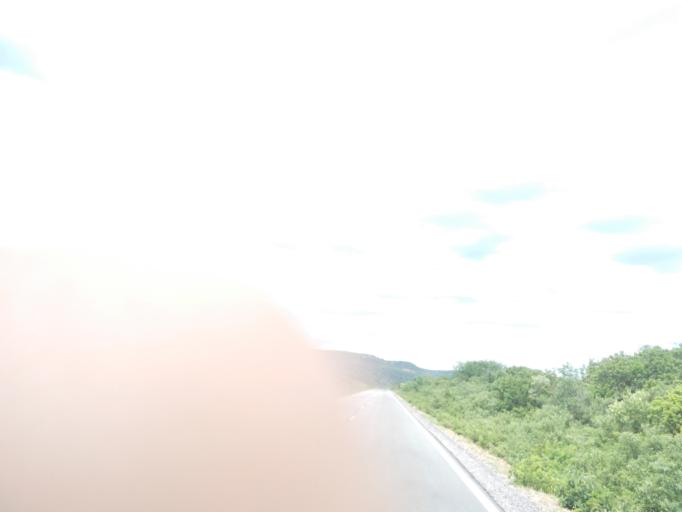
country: BR
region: Piaui
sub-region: Sao Raimundo Nonato
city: Sao Raimundo Nonato
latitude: -8.8085
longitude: -42.4707
